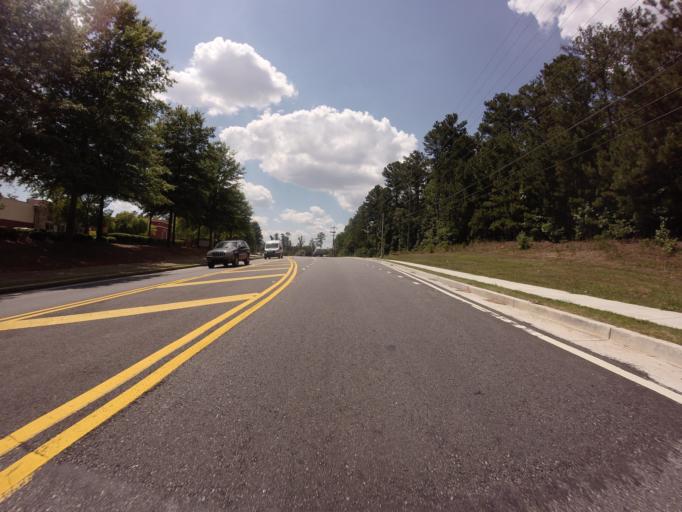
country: US
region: Georgia
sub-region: Fulton County
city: Johns Creek
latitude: 34.0236
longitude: -84.2509
